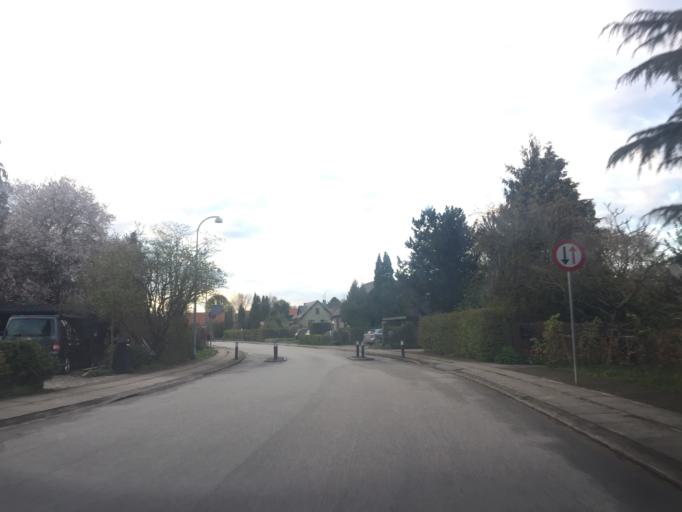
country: DK
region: Capital Region
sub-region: Rodovre Kommune
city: Rodovre
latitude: 55.6545
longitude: 12.4439
